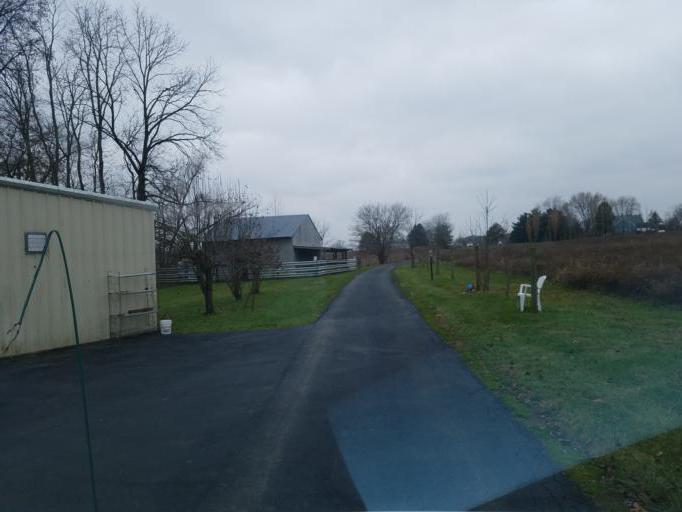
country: US
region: Ohio
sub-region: Morrow County
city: Cardington
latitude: 40.4290
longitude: -82.8492
